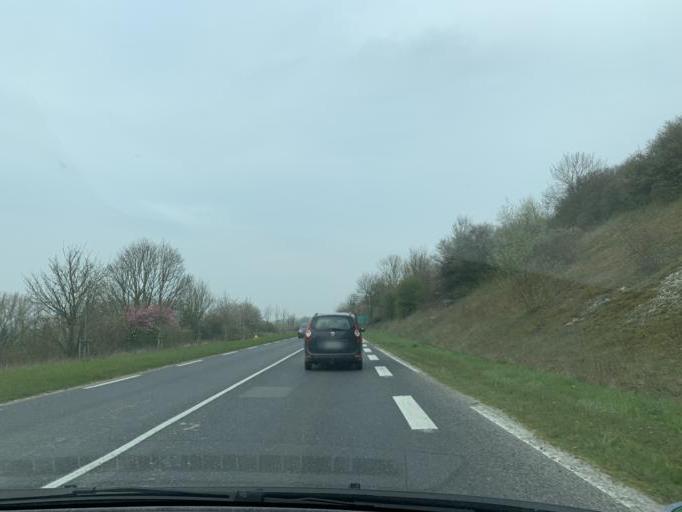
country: FR
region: Nord-Pas-de-Calais
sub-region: Departement du Pas-de-Calais
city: Montreuil
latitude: 50.4587
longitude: 1.7709
